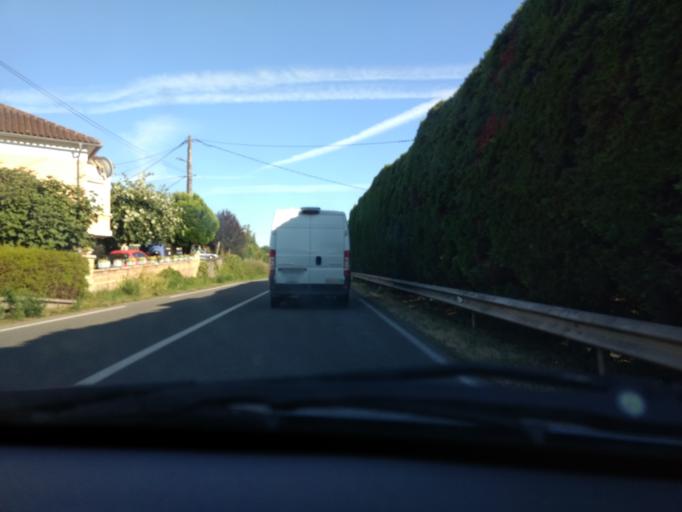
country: FR
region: Midi-Pyrenees
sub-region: Departement de l'Aveyron
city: Firmi
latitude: 44.5445
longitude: 2.3048
